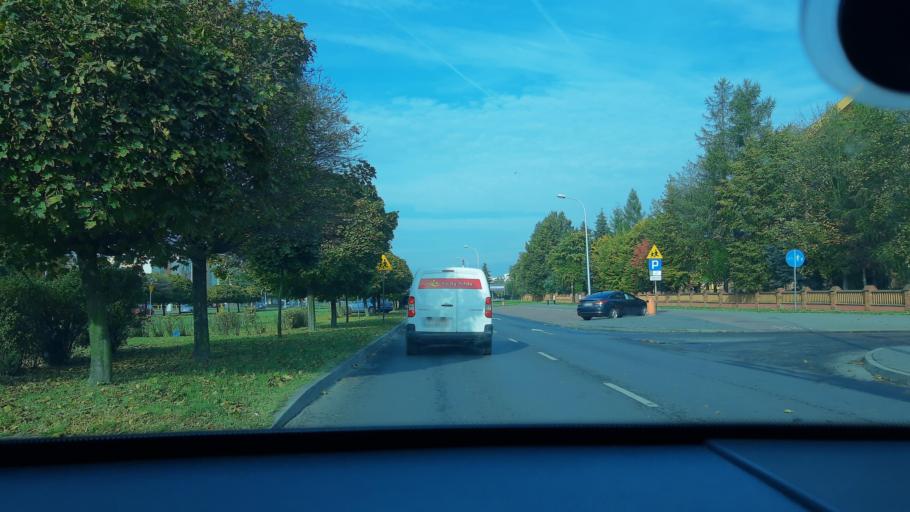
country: PL
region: Lodz Voivodeship
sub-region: Powiat sieradzki
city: Sieradz
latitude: 51.5892
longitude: 18.7187
